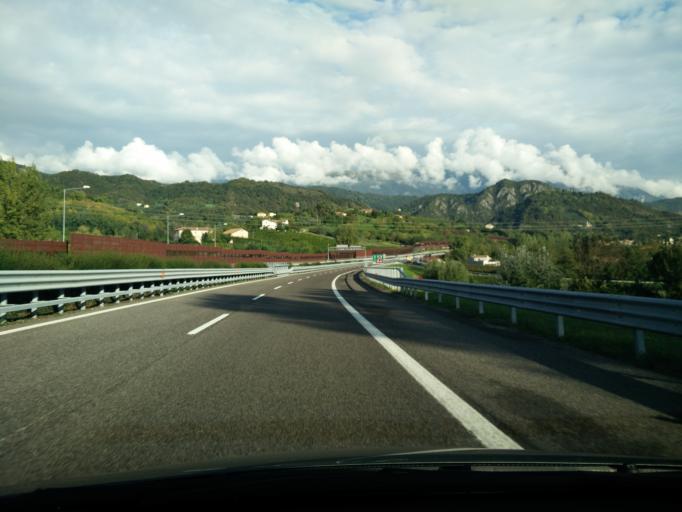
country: IT
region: Veneto
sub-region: Provincia di Treviso
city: Carpesica
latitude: 45.9622
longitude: 12.2870
